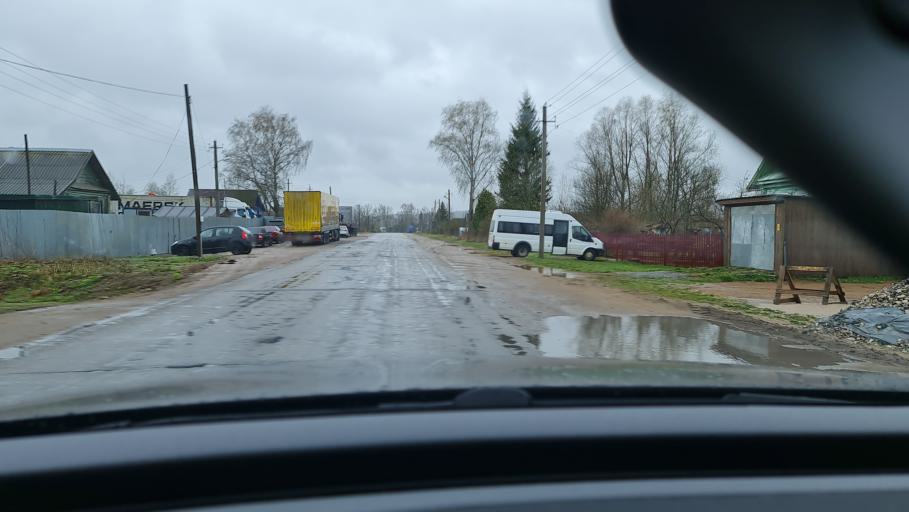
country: RU
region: Novgorod
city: Valday
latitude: 58.0336
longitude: 32.9667
